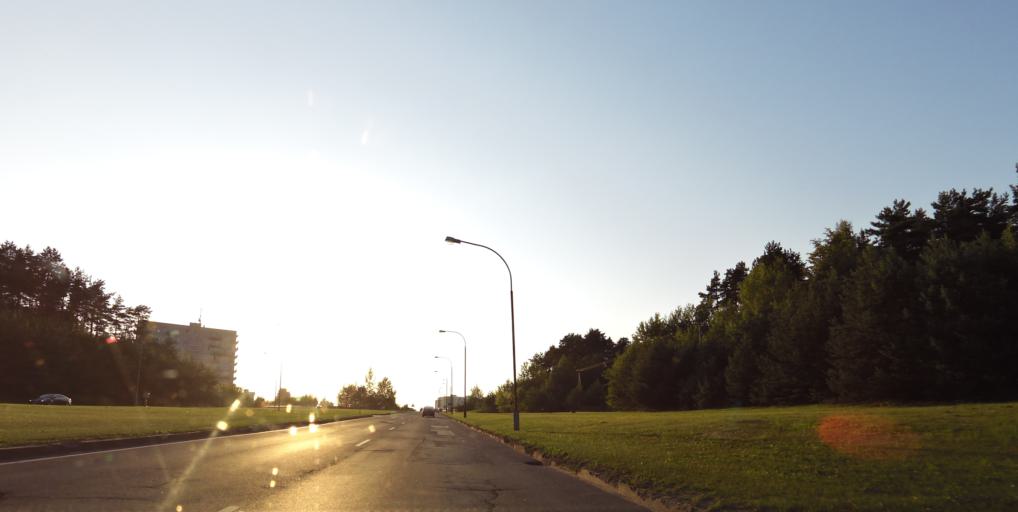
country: LT
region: Vilnius County
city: Pilaite
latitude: 54.7073
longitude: 25.1936
